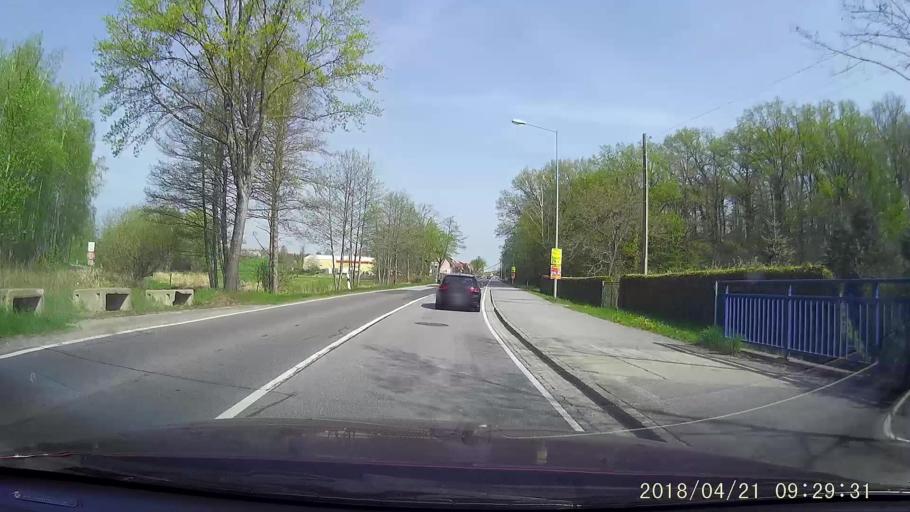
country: DE
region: Saxony
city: Bautzen
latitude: 51.1929
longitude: 14.4100
